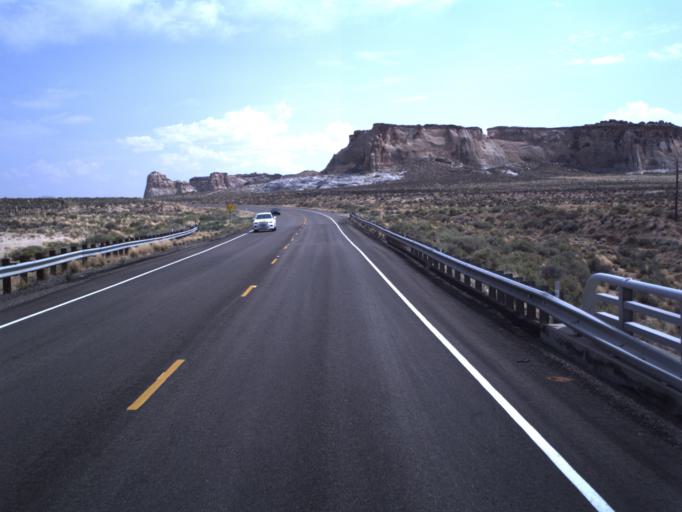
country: US
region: Arizona
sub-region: Coconino County
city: Page
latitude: 37.0386
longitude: -111.6174
